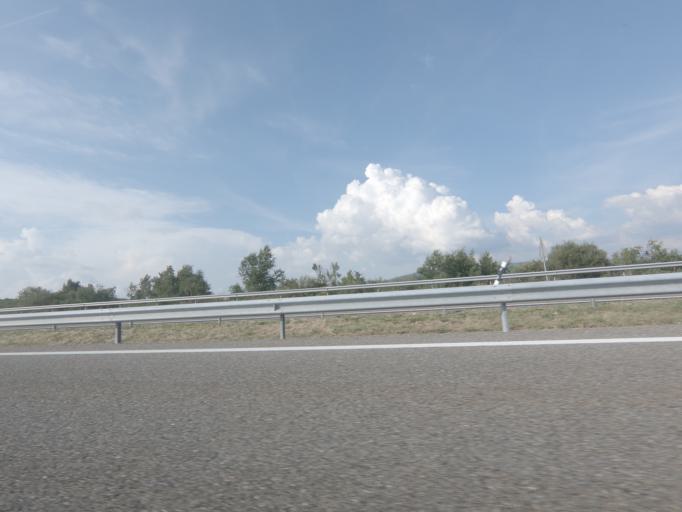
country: ES
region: Galicia
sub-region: Provincia de Ourense
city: Cualedro
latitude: 41.9869
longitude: -7.5505
